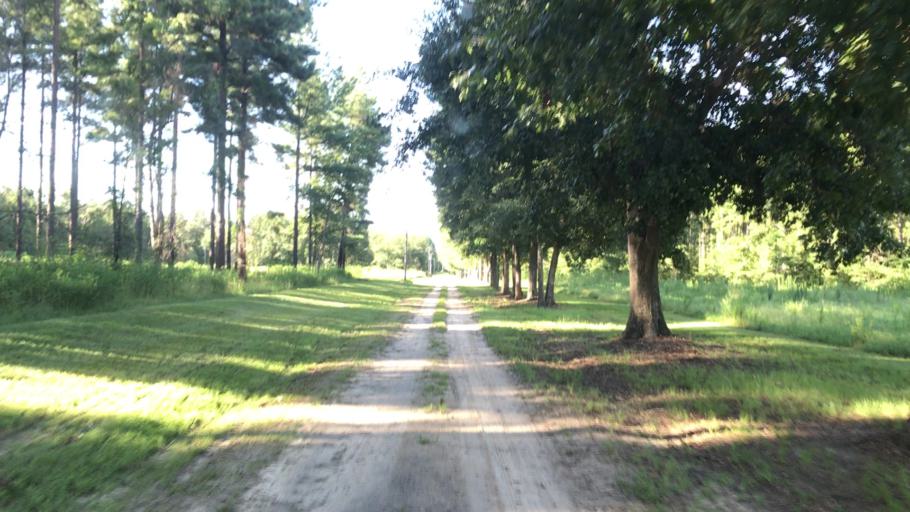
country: US
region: Georgia
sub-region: Jefferson County
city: Wadley
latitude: 32.8137
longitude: -82.3339
